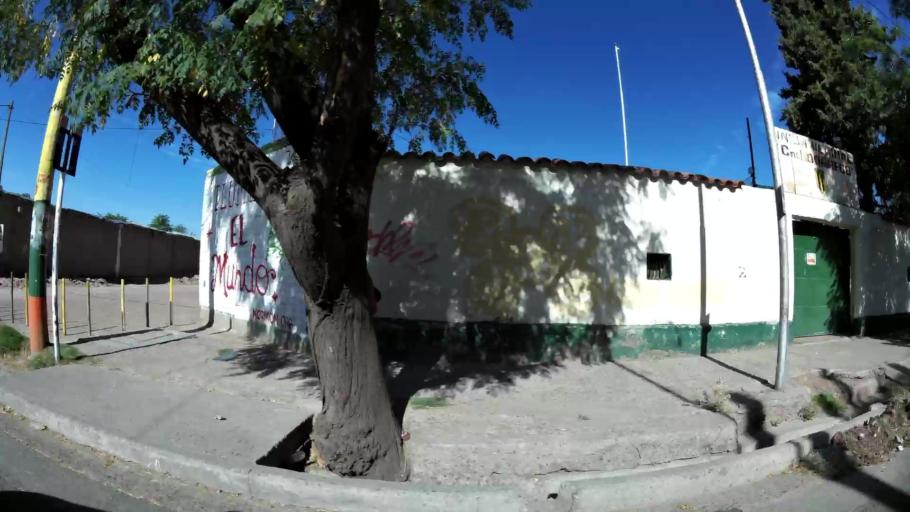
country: AR
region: Mendoza
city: Mendoza
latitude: -32.9045
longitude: -68.8306
